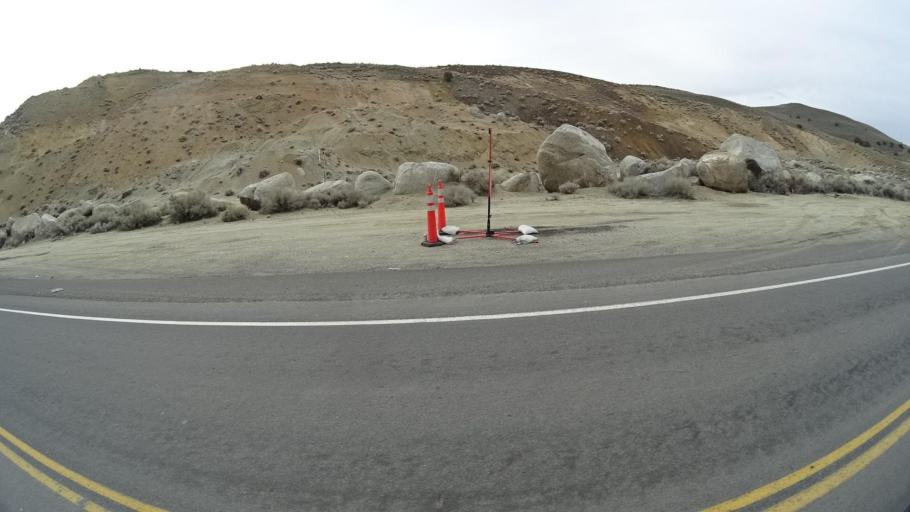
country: US
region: Nevada
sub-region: Washoe County
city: Sun Valley
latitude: 39.6095
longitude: -119.7411
